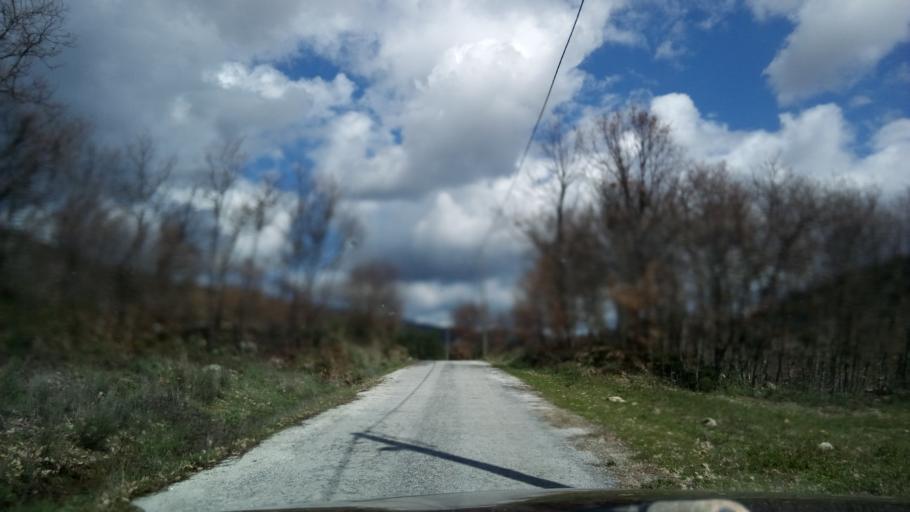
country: PT
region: Guarda
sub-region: Fornos de Algodres
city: Fornos de Algodres
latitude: 40.6467
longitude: -7.5050
